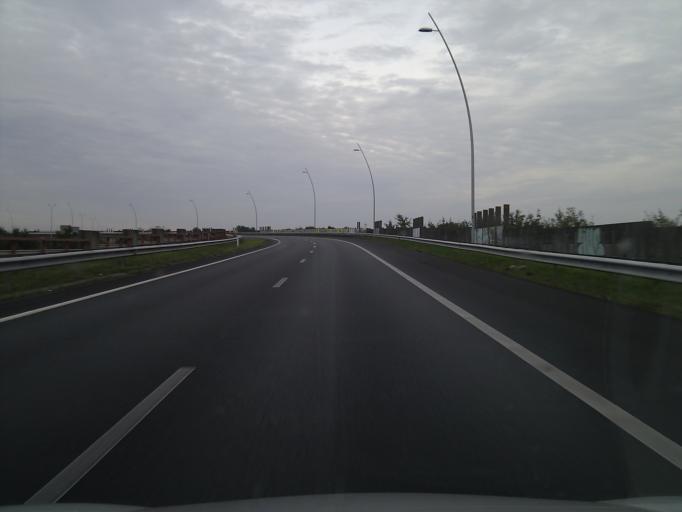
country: NL
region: North Brabant
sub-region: Gemeente Best
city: Best
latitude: 51.4878
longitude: 5.4262
